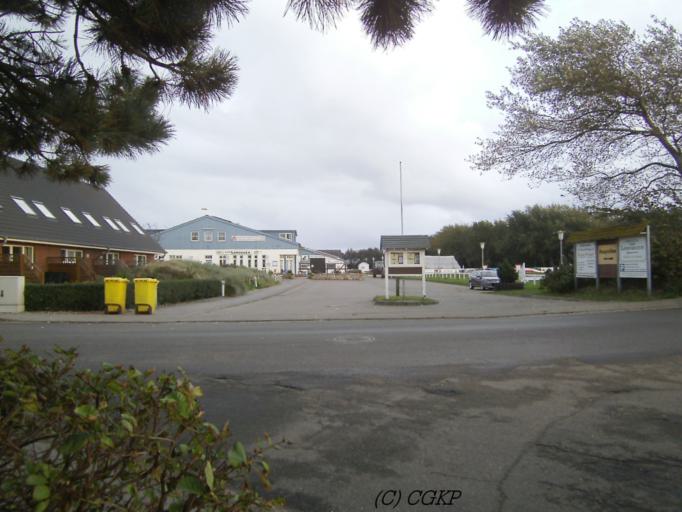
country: DE
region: Schleswig-Holstein
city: Sankt Peter-Ording
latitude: 54.3033
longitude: 8.6323
